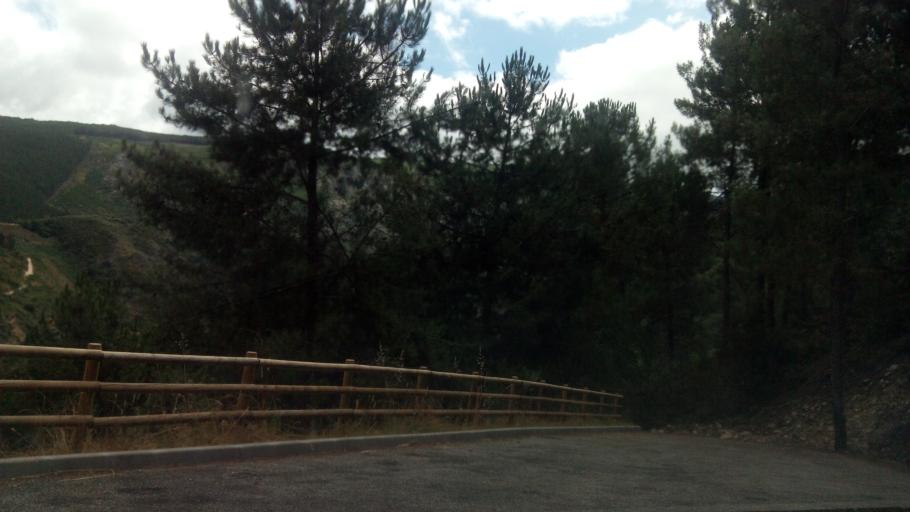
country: ES
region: Galicia
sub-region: Provincia de Ourense
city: Luintra
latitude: 42.4090
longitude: -7.6470
